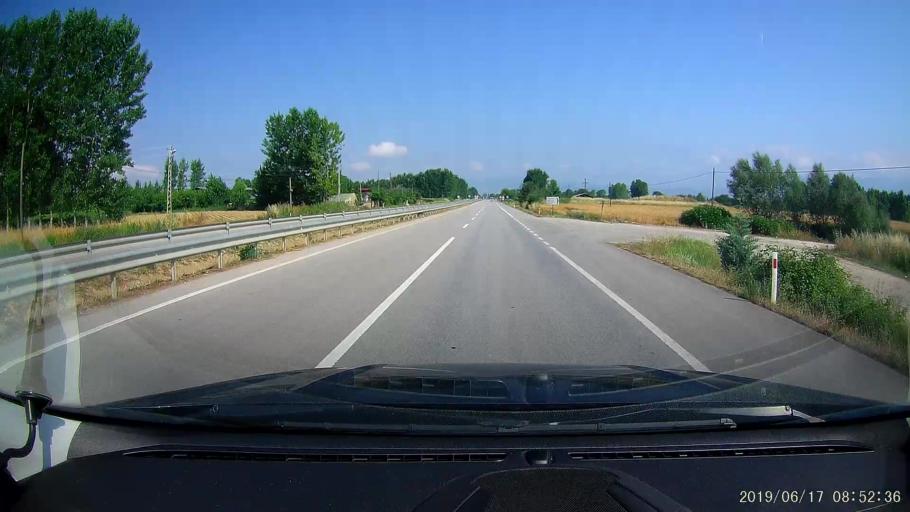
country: TR
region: Tokat
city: Erbaa
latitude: 40.6999
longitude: 36.4941
